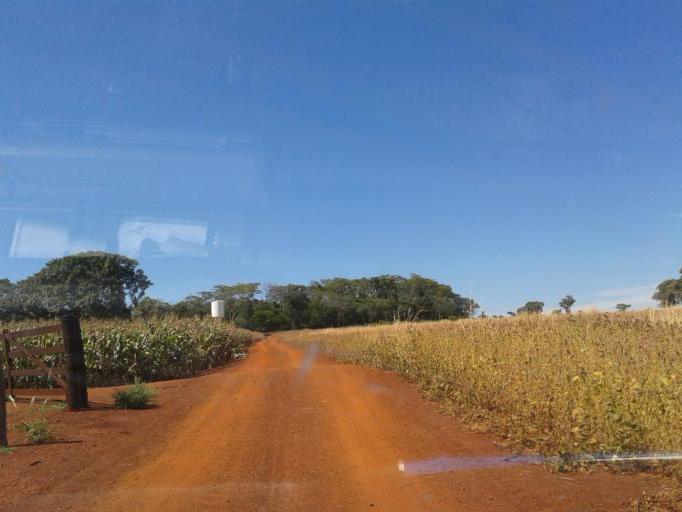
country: BR
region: Minas Gerais
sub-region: Capinopolis
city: Capinopolis
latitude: -18.6091
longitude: -49.6137
